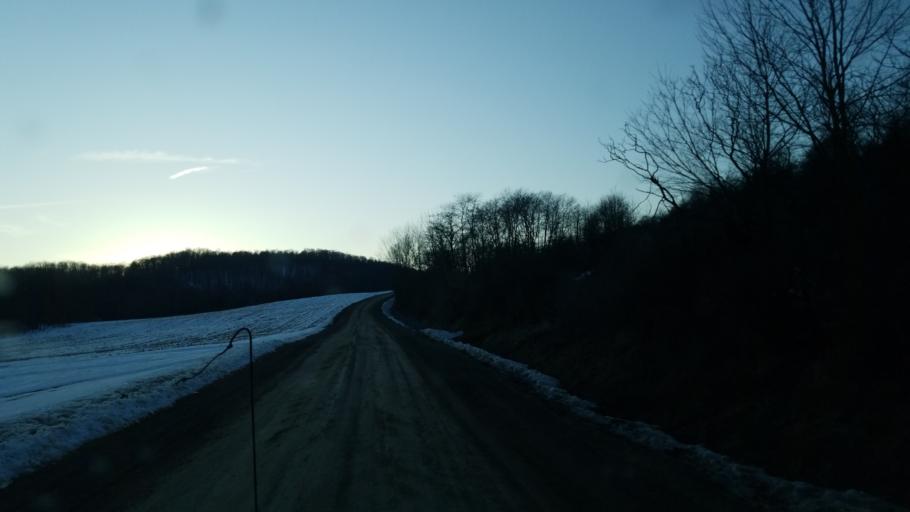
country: US
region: Pennsylvania
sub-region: Tioga County
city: Westfield
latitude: 42.0369
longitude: -77.5817
